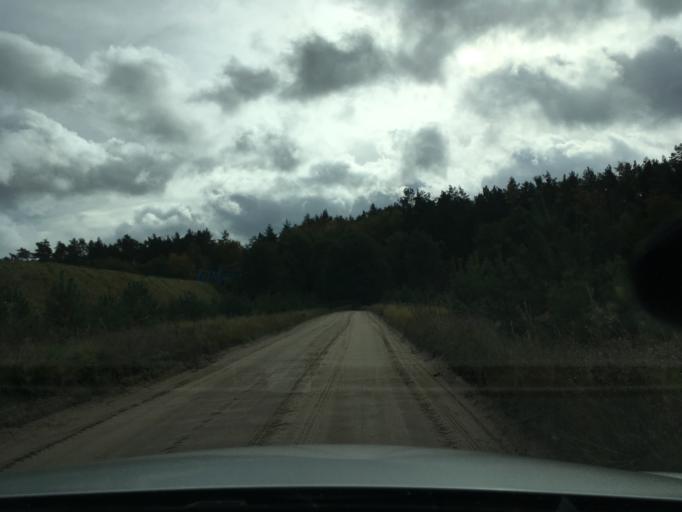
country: PL
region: Pomeranian Voivodeship
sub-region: Powiat koscierski
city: Koscierzyna
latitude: 54.1065
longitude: 18.0125
